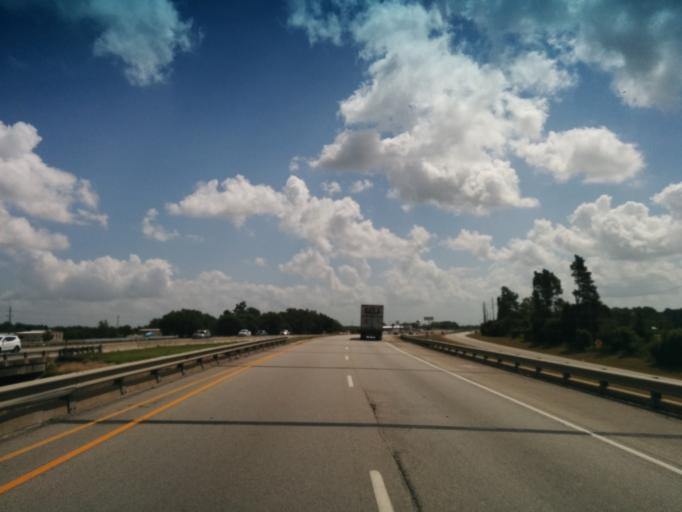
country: US
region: Texas
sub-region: Austin County
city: Sealy
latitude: 29.7731
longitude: -96.1342
